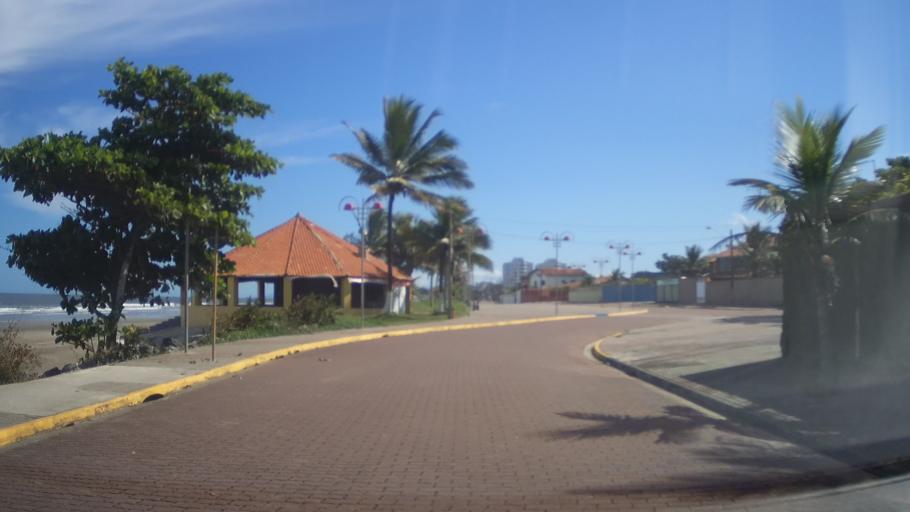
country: BR
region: Sao Paulo
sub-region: Itanhaem
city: Itanhaem
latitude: -24.1726
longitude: -46.7622
